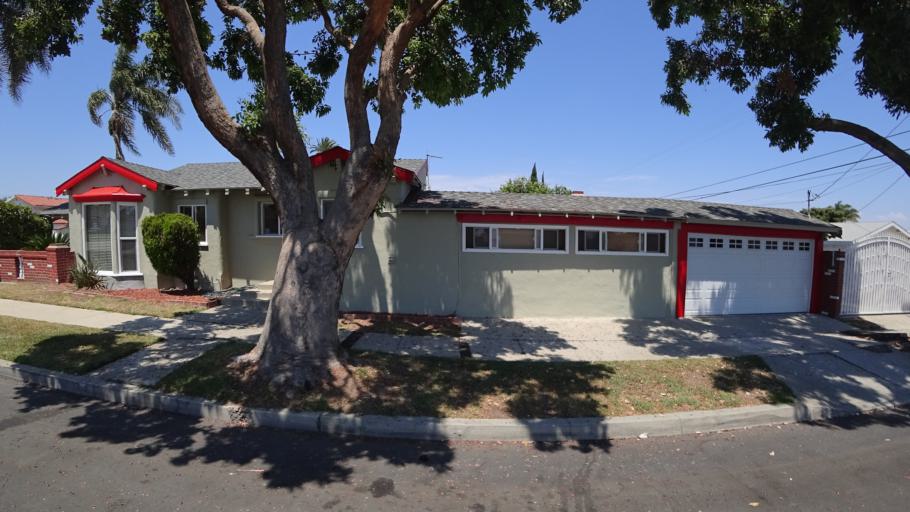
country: US
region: California
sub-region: Los Angeles County
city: Westmont
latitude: 33.9545
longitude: -118.3032
